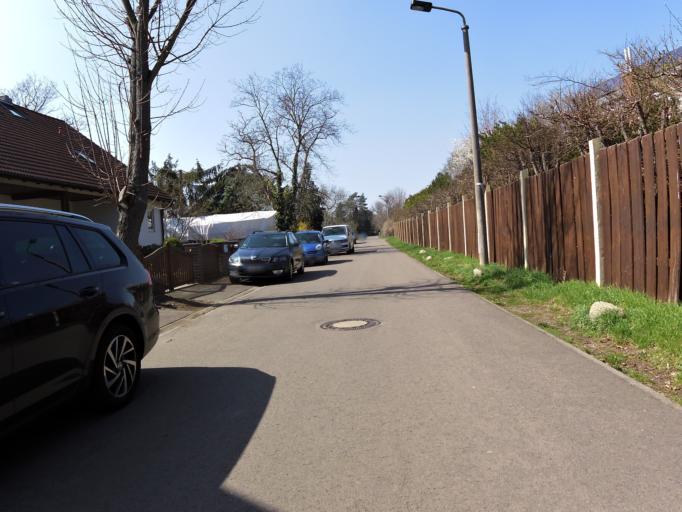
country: DE
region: Saxony
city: Leipzig
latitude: 51.3752
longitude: 12.3112
